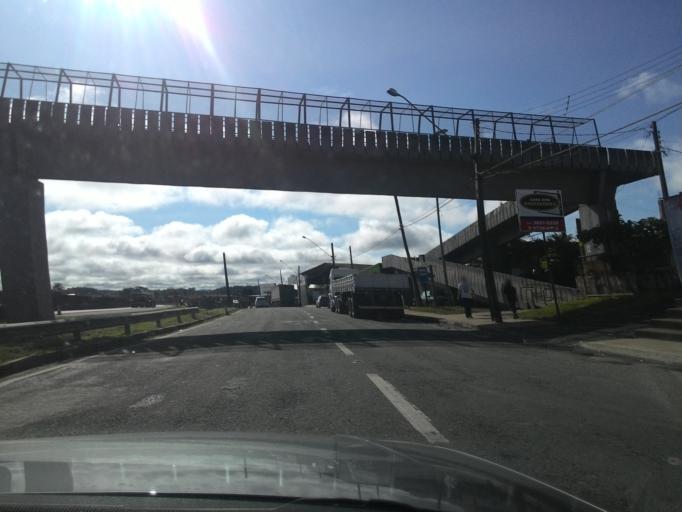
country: BR
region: Sao Paulo
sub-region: Registro
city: Registro
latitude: -24.4943
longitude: -47.8381
